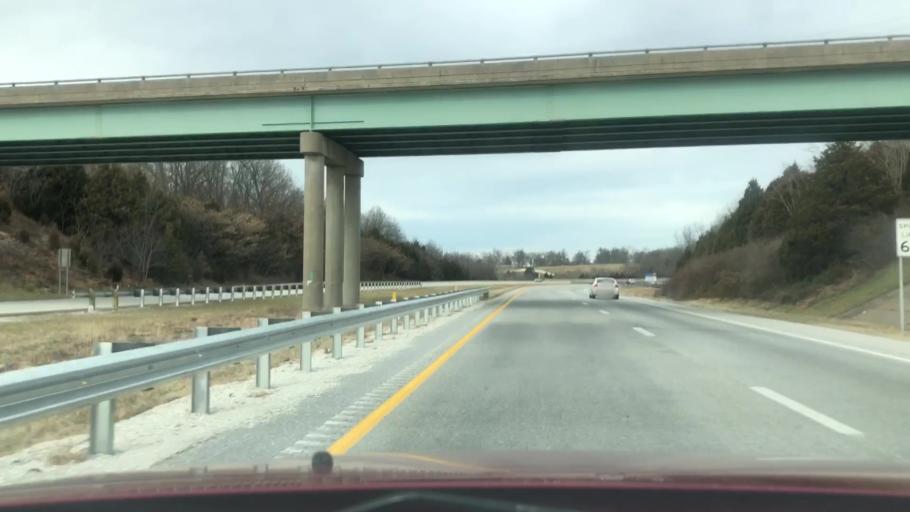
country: US
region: Missouri
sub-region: Greene County
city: Springfield
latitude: 37.2605
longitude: -93.2248
